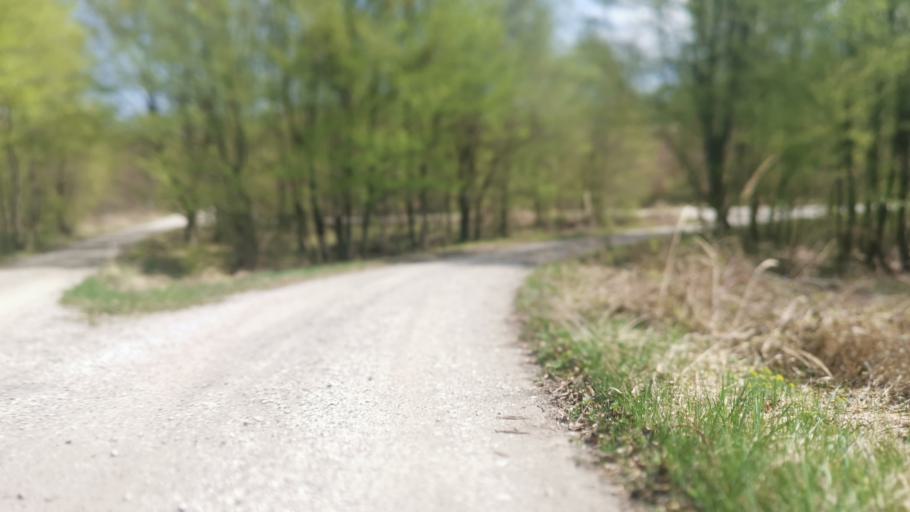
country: SK
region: Nitriansky
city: Brezova pod Bradlom
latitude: 48.5974
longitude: 17.4940
